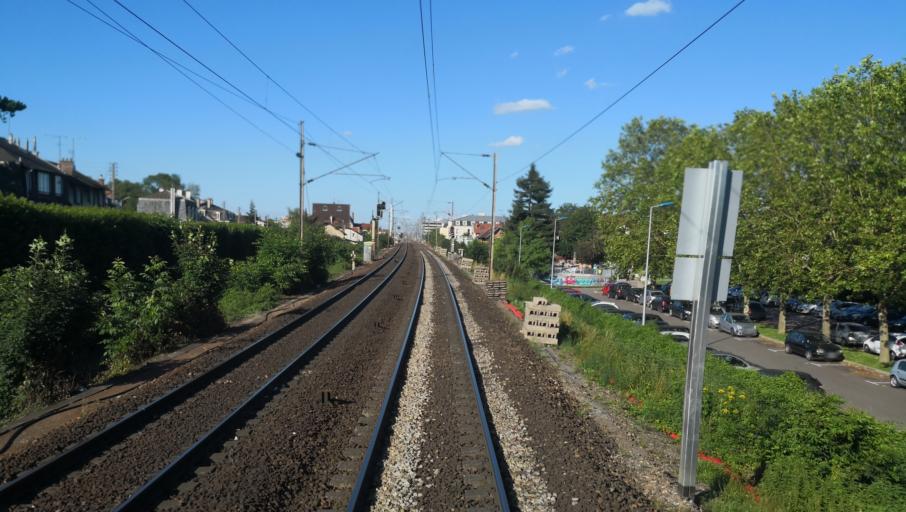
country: FR
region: Ile-de-France
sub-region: Departement des Yvelines
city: Poissy
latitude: 48.9296
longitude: 2.0328
